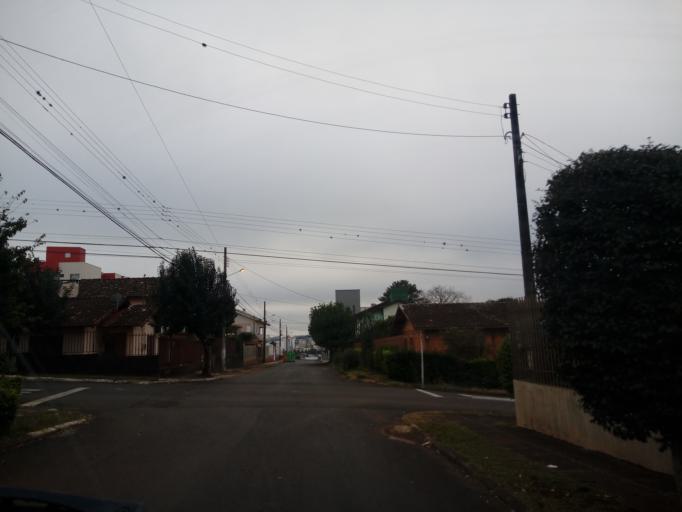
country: BR
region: Santa Catarina
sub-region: Chapeco
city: Chapeco
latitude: -27.0909
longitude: -52.6288
